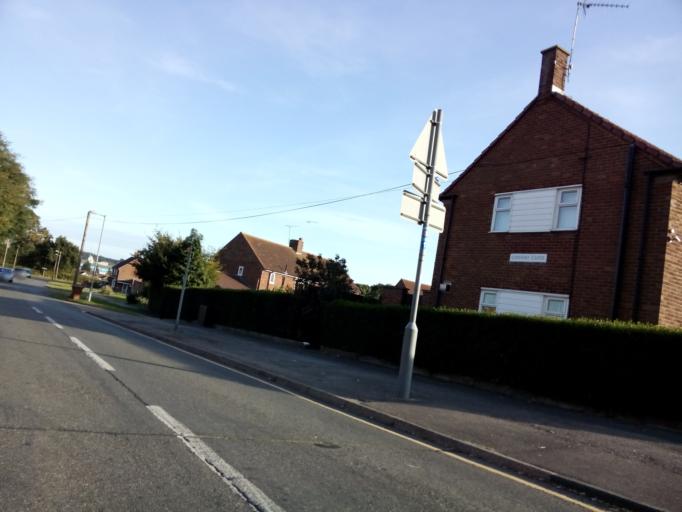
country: GB
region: England
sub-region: Suffolk
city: Ipswich
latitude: 52.0416
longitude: 1.1465
